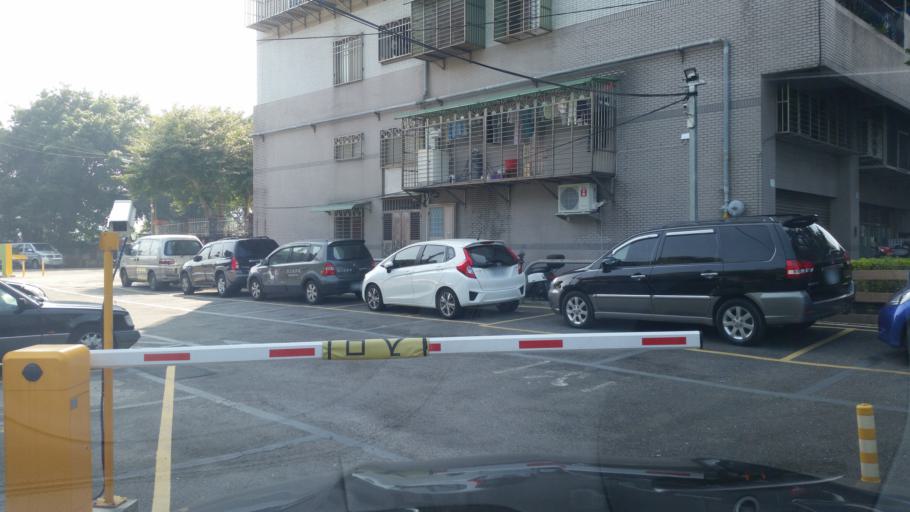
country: TW
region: Taipei
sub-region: Taipei
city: Banqiao
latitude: 24.9864
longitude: 121.5220
